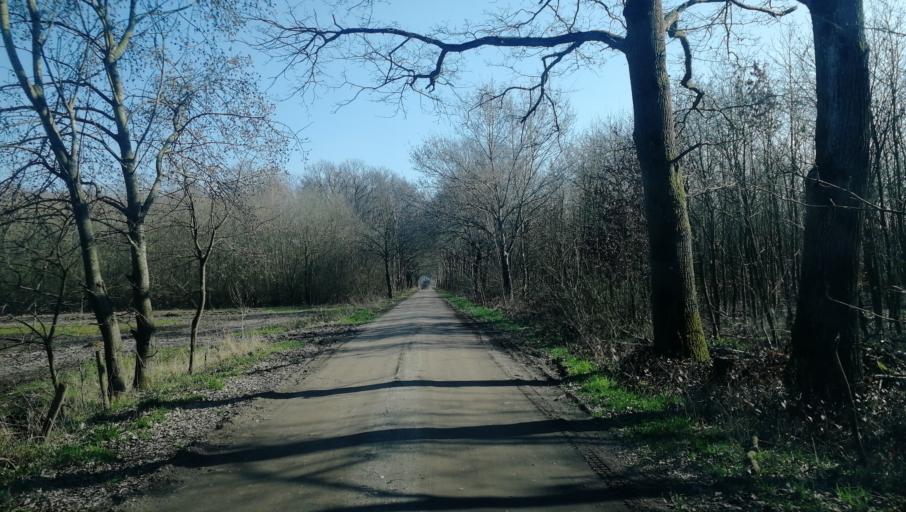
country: NL
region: Limburg
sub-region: Gemeente Venlo
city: Venlo
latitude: 51.4008
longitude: 6.1998
